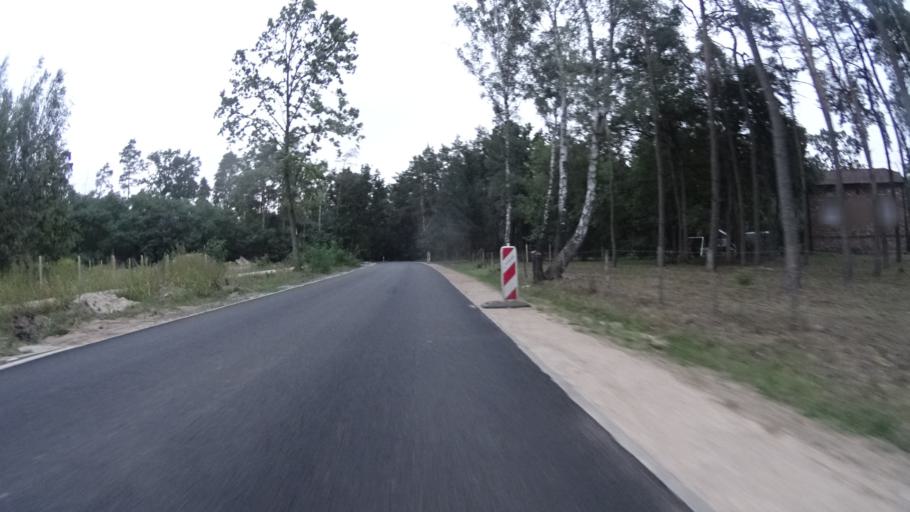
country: PL
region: Masovian Voivodeship
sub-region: Powiat warszawski zachodni
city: Stare Babice
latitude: 52.2710
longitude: 20.8332
